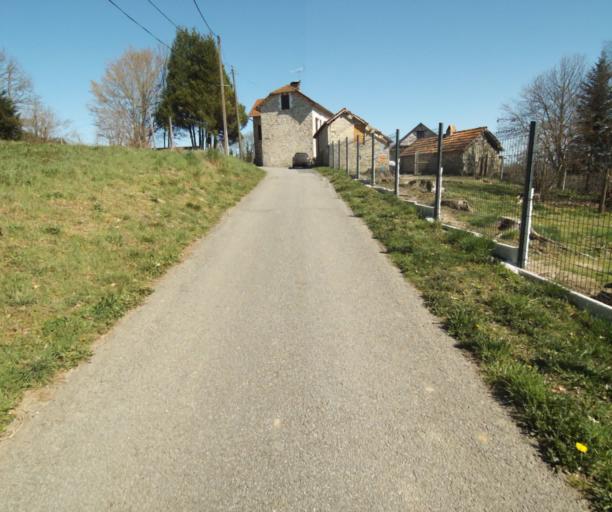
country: FR
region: Limousin
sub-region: Departement de la Correze
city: Chameyrat
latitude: 45.2449
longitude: 1.7004
